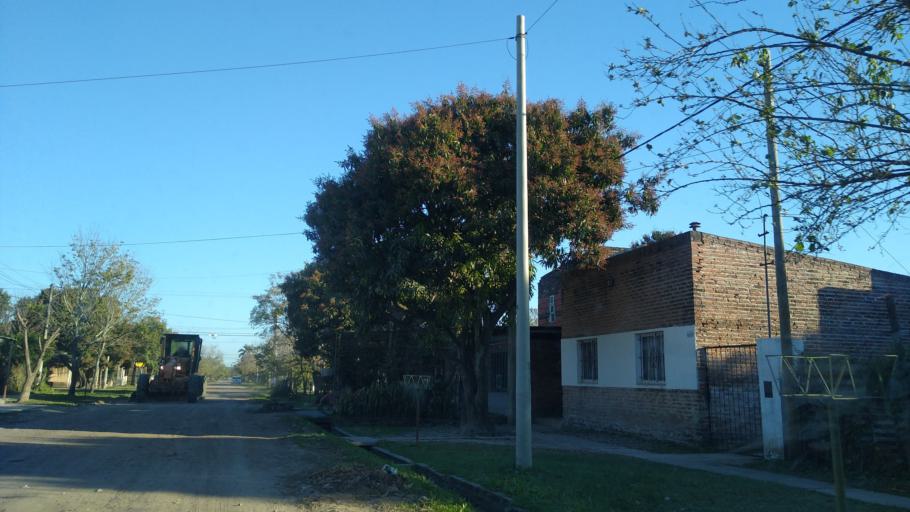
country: AR
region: Chaco
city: Resistencia
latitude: -27.4800
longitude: -58.9654
